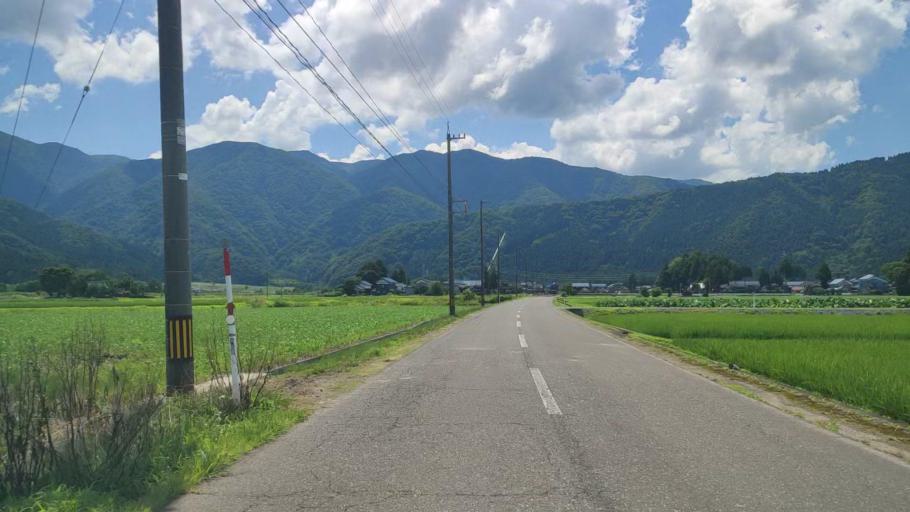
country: JP
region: Fukui
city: Ono
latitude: 35.9465
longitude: 136.5433
